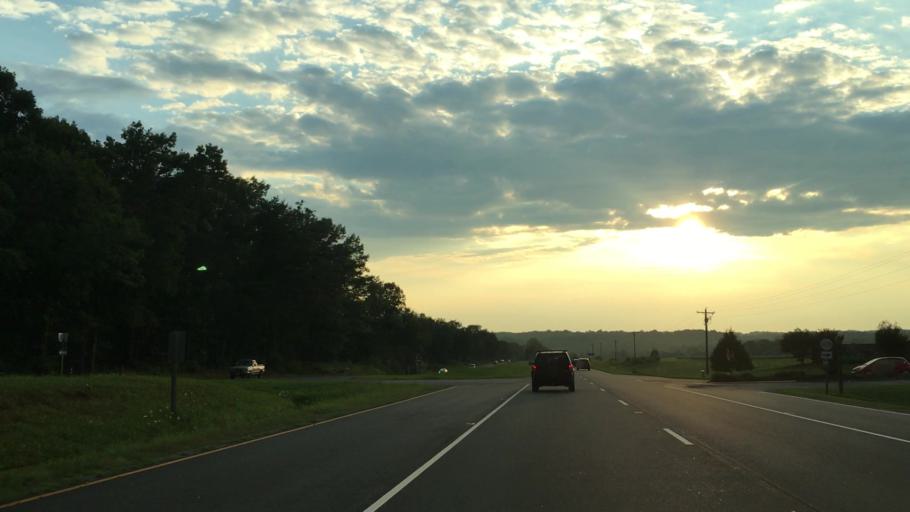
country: US
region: Virginia
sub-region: Spotsylvania County
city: Spotsylvania
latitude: 38.3237
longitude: -77.7139
